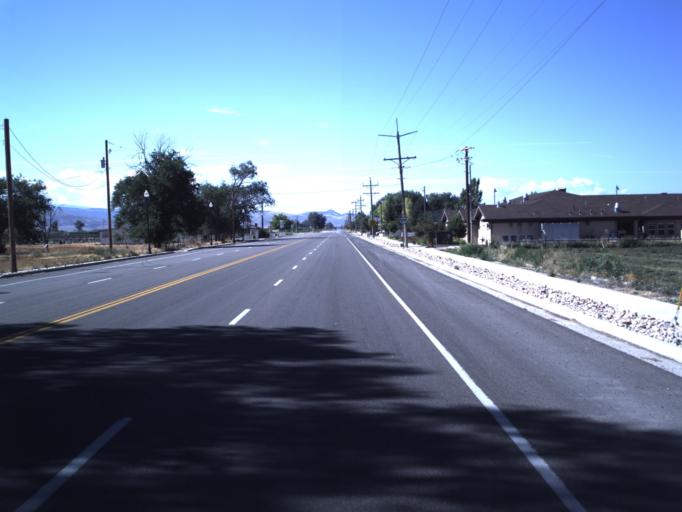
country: US
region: Utah
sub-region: Sanpete County
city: Centerfield
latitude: 39.1208
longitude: -111.8194
